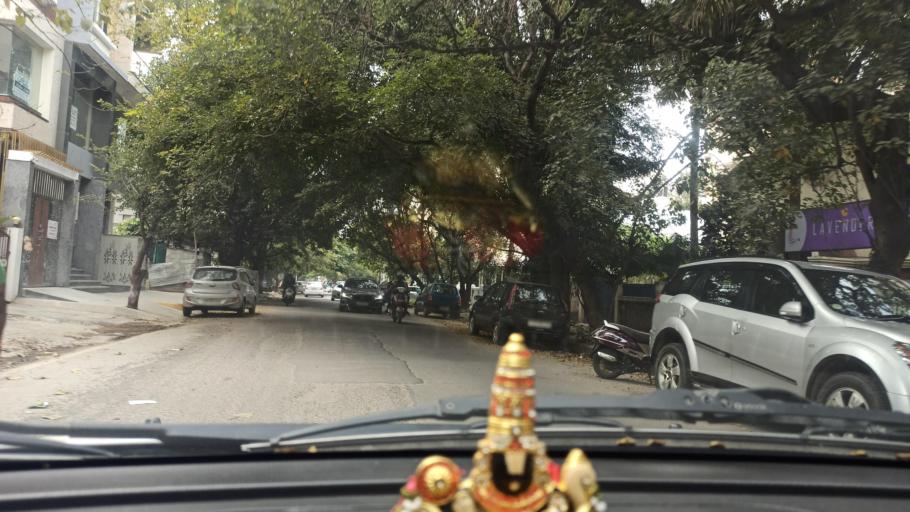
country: IN
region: Karnataka
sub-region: Bangalore Urban
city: Bangalore
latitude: 13.0181
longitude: 77.6471
